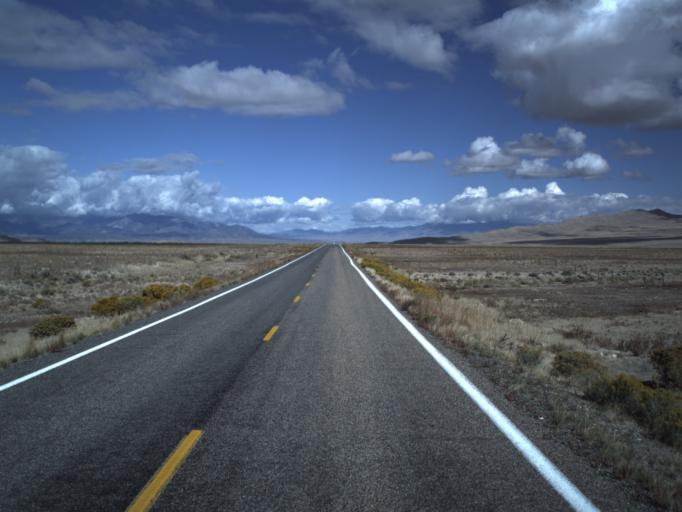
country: US
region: Utah
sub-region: Beaver County
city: Milford
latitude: 38.6641
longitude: -113.8796
